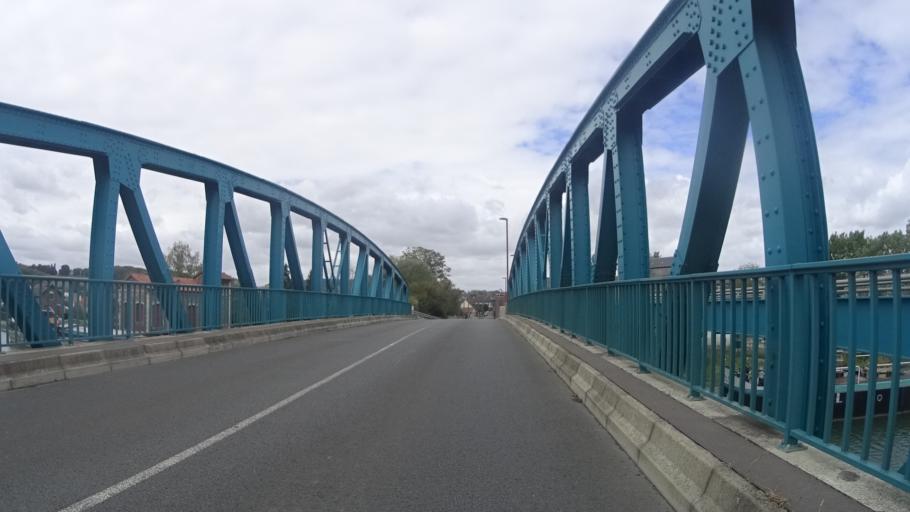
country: FR
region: Picardie
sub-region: Departement de l'Oise
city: Noyon
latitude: 49.5616
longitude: 2.9918
